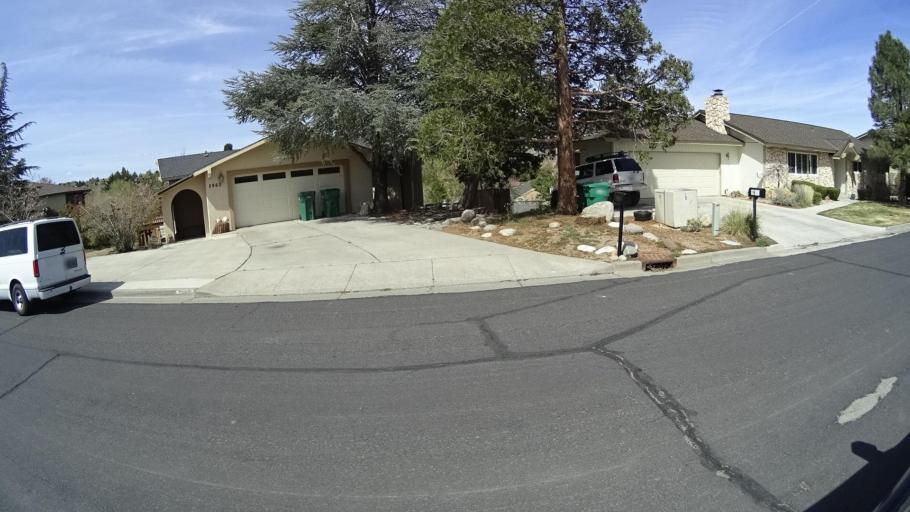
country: US
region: Nevada
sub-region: Washoe County
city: Reno
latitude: 39.4970
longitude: -119.8410
